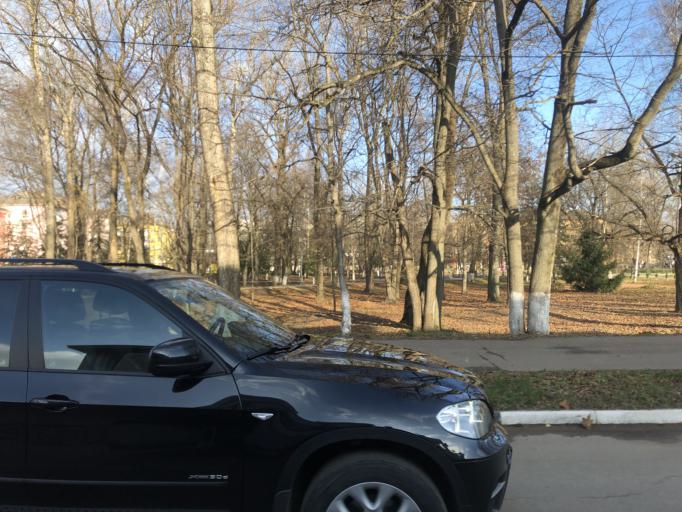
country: RU
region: Tverskaya
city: Rzhev
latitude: 56.2627
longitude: 34.3322
